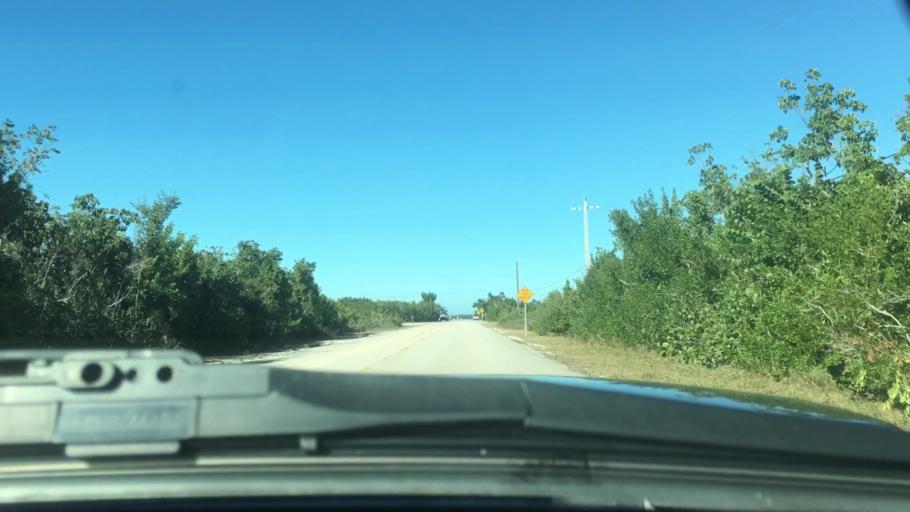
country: US
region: Florida
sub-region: Monroe County
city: Cudjoe Key
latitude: 24.6917
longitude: -81.4996
